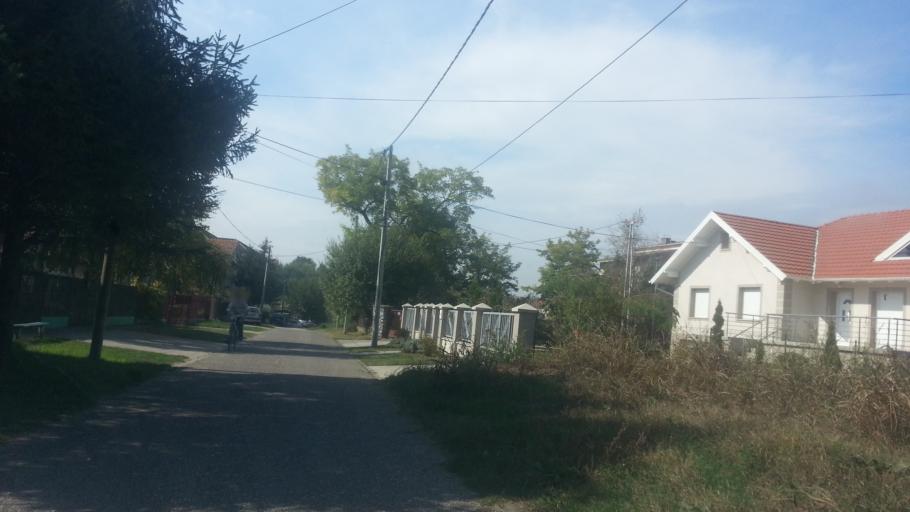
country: RS
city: Stari Banovci
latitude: 44.9861
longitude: 20.2817
